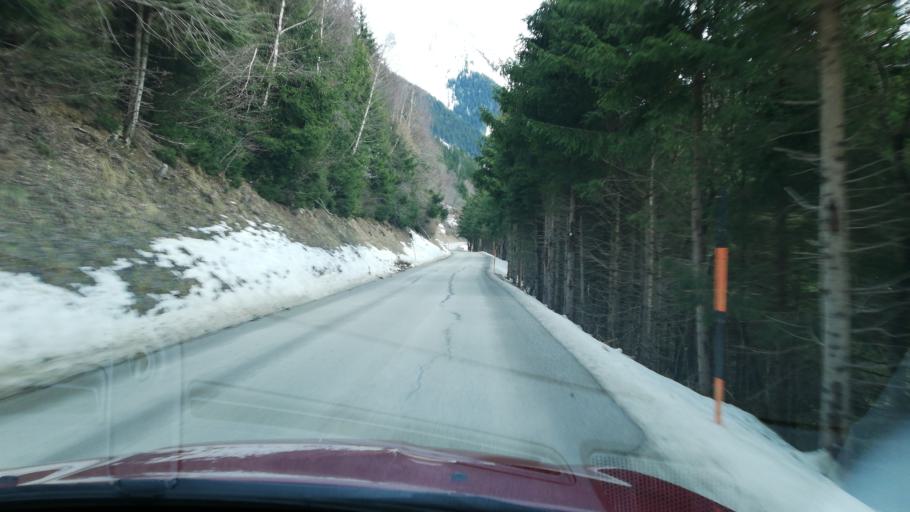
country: AT
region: Styria
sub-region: Politischer Bezirk Liezen
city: Donnersbach
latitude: 47.4382
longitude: 14.1446
